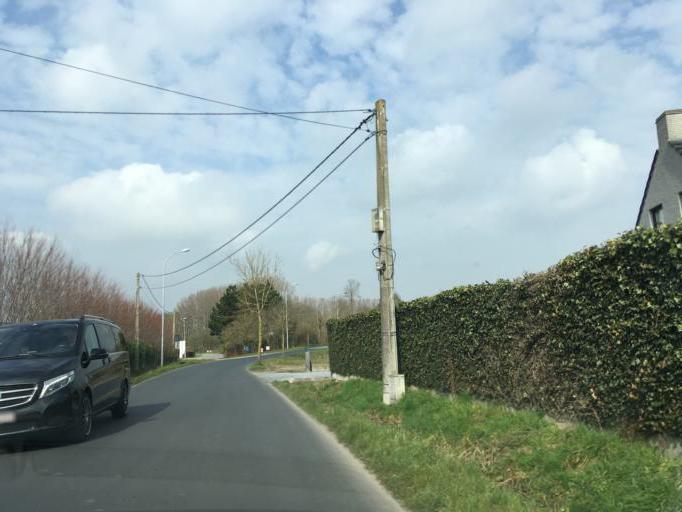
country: BE
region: Flanders
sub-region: Provincie West-Vlaanderen
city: Ardooie
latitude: 50.9431
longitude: 3.1787
